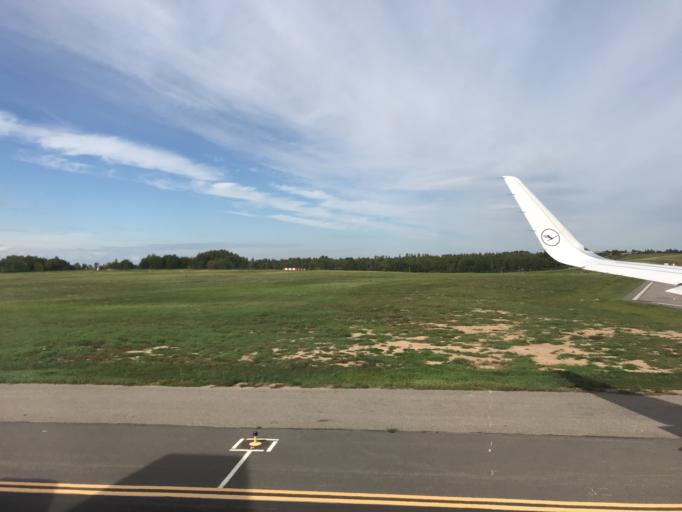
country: LT
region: Vilnius County
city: Rasos
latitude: 54.6432
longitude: 25.2909
